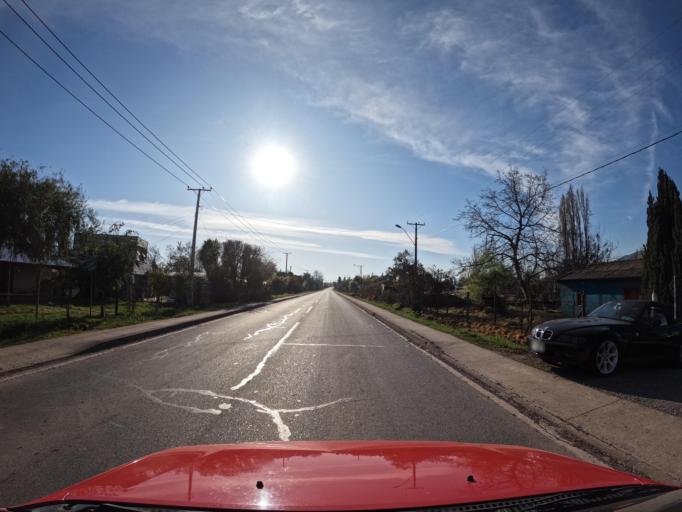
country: CL
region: Maule
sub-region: Provincia de Curico
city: Teno
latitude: -34.9558
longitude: -70.9778
